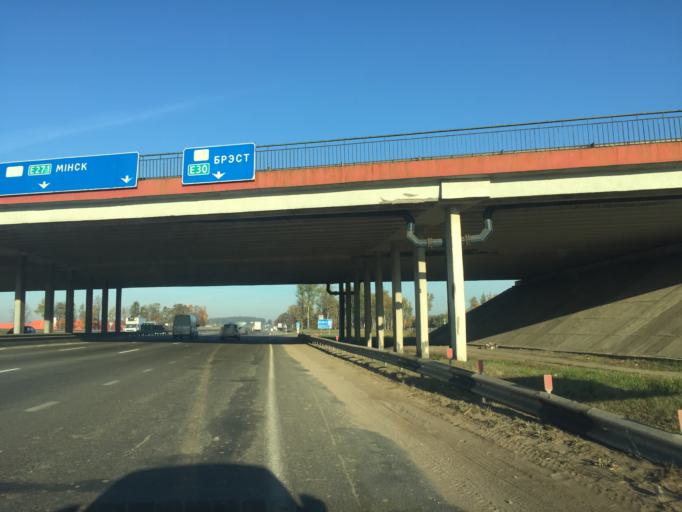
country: BY
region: Minsk
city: Pryvol'ny
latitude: 53.8043
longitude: 27.7949
